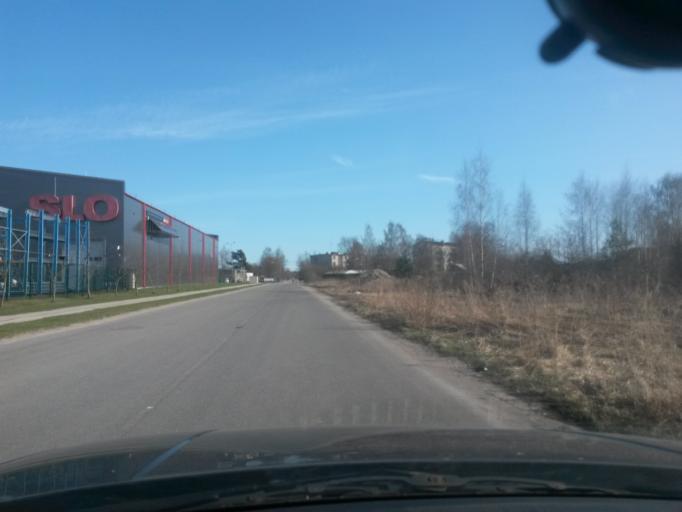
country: LV
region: Stopini
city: Ulbroka
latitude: 56.9087
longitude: 24.2182
